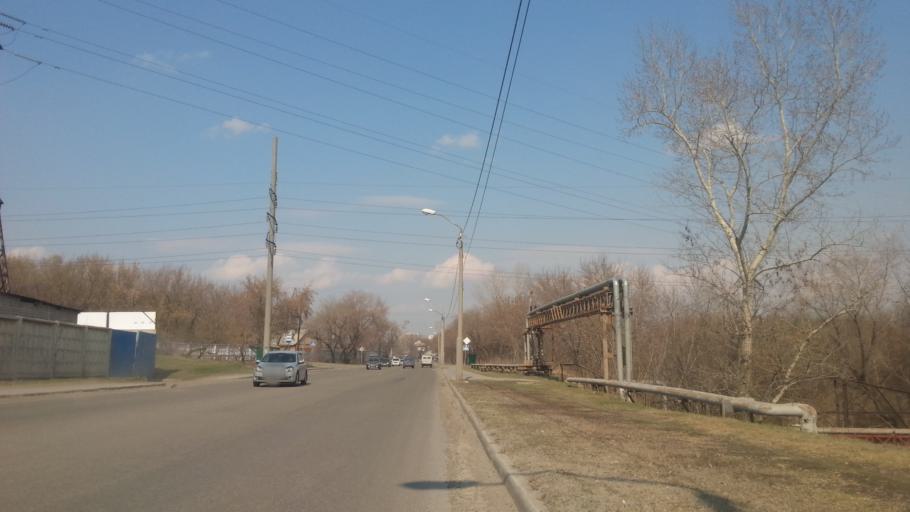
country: RU
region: Altai Krai
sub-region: Gorod Barnaulskiy
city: Barnaul
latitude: 53.3194
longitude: 83.7621
